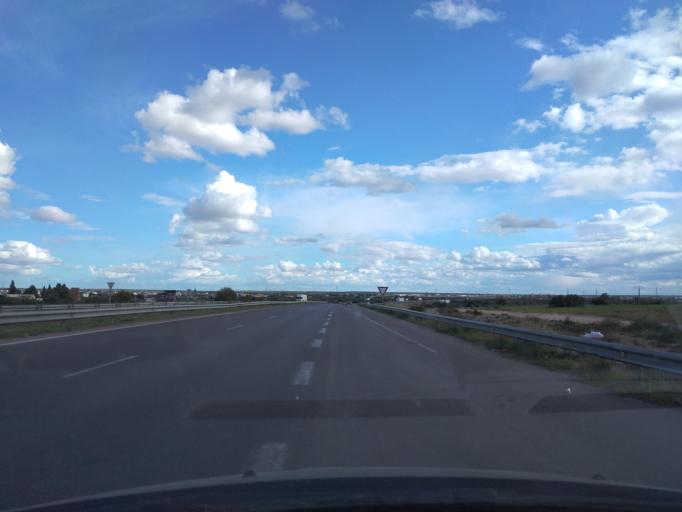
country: TN
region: Susah
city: Masakin
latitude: 35.7099
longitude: 10.5602
